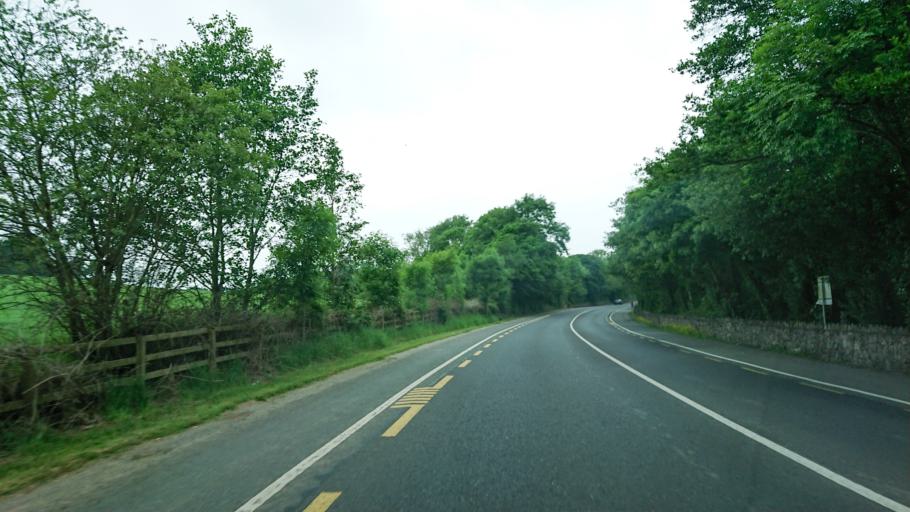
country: IE
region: Munster
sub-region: Waterford
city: Waterford
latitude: 52.2154
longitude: -7.1251
